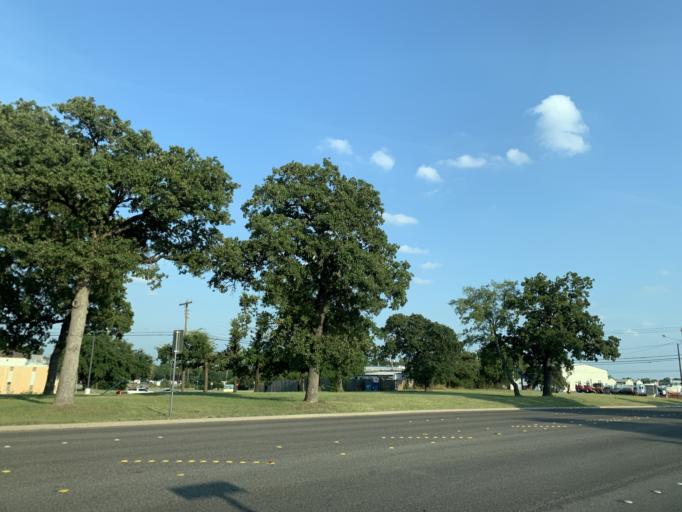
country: US
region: Texas
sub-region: Tarrant County
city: Hurst
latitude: 32.8100
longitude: -97.1692
